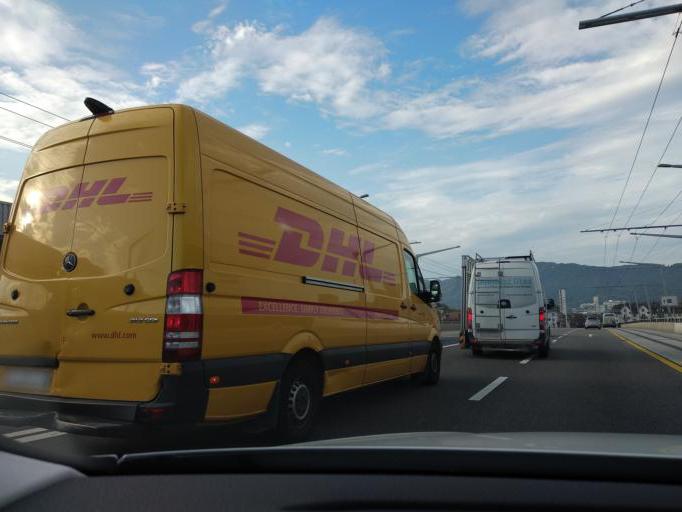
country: CH
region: Zurich
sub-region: Bezirk Zuerich
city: Zuerich (Kreis 5)
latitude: 47.3850
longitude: 8.5168
